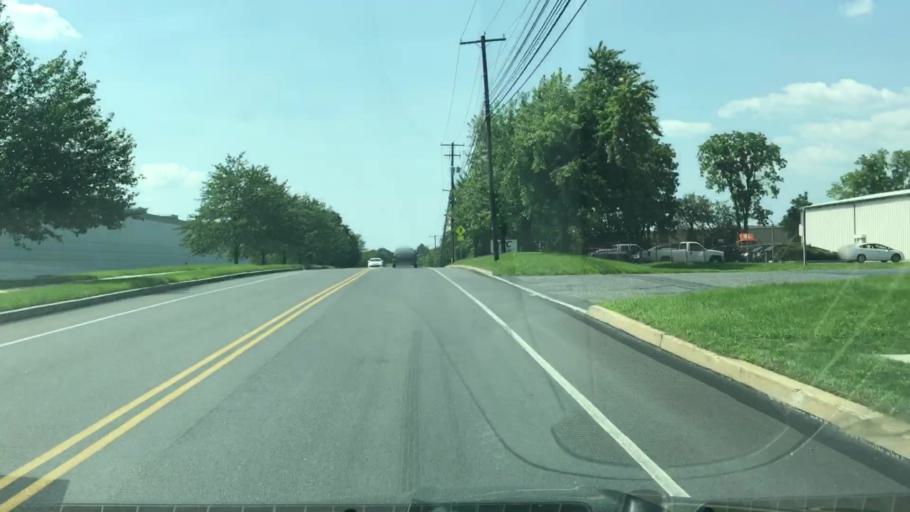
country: US
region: Pennsylvania
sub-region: Northampton County
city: Middletown
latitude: 40.6790
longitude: -75.3609
